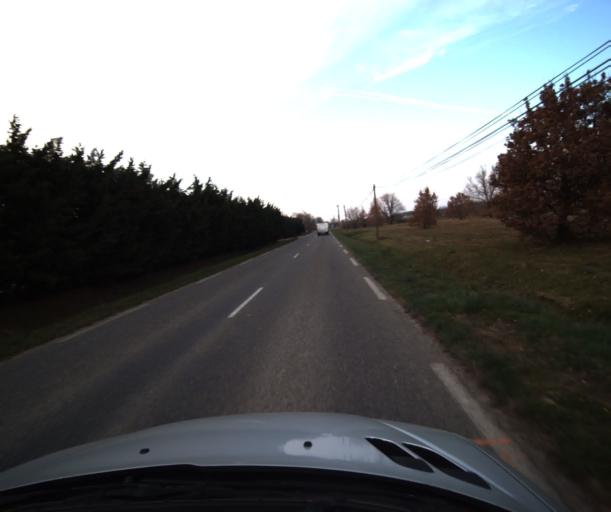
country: FR
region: Midi-Pyrenees
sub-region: Departement de la Haute-Garonne
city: Fronton
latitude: 43.8613
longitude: 1.3832
